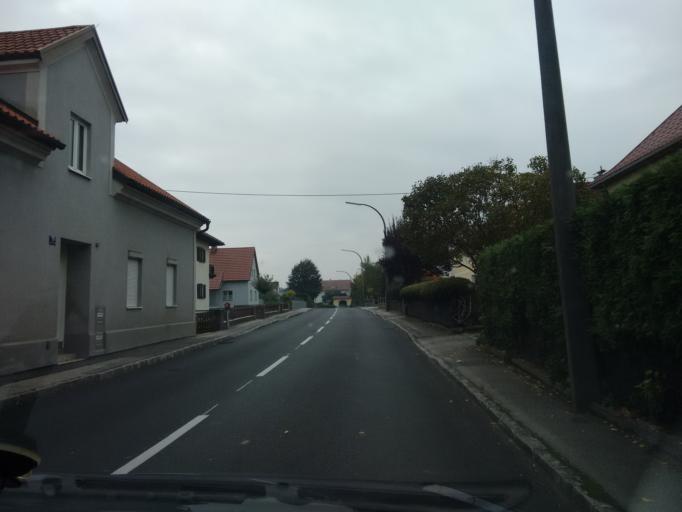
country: AT
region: Upper Austria
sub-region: Politischer Bezirk Steyr-Land
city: Bad Hall
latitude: 48.0296
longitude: 14.2169
